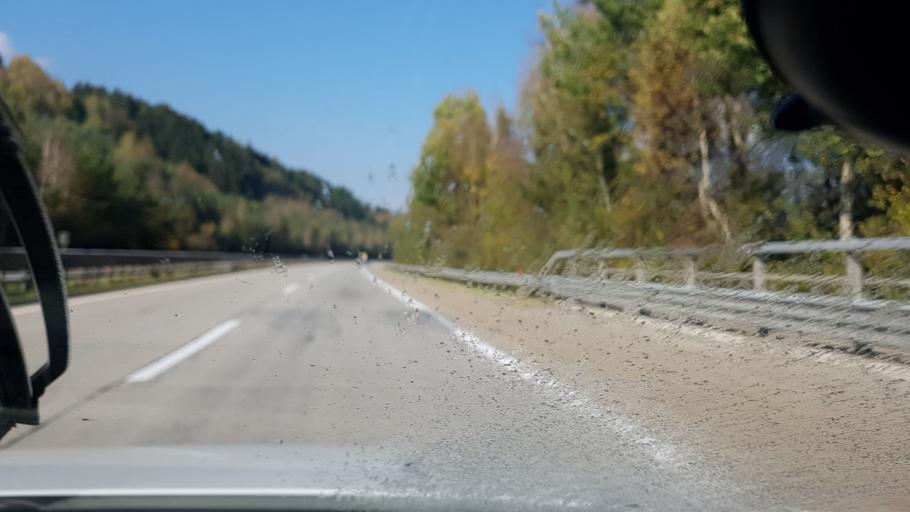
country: AT
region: Carinthia
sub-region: Politischer Bezirk Villach Land
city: Ferndorf
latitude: 46.7443
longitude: 13.5816
